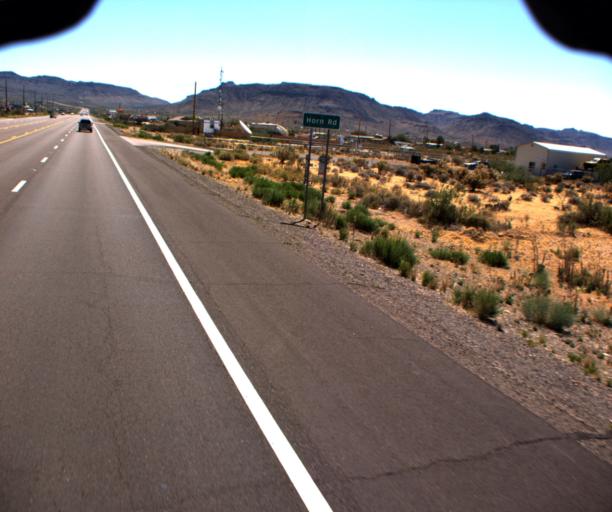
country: US
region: Arizona
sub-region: Mohave County
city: Golden Valley
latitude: 35.2199
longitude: -114.1740
